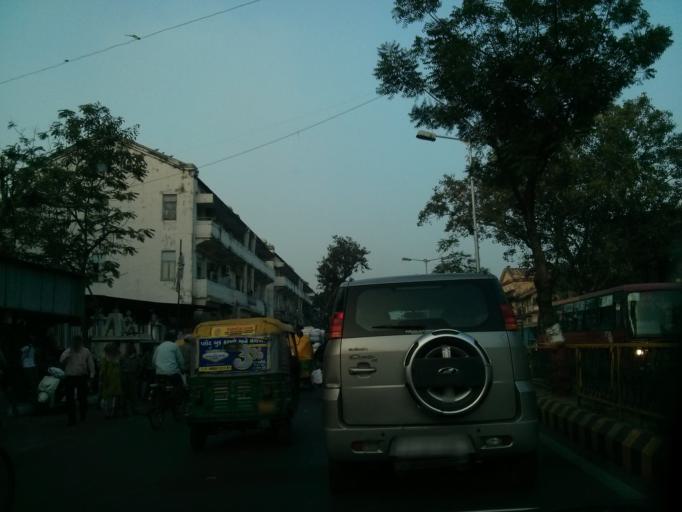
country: IN
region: Gujarat
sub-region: Ahmadabad
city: Ahmedabad
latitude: 23.0396
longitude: 72.5883
